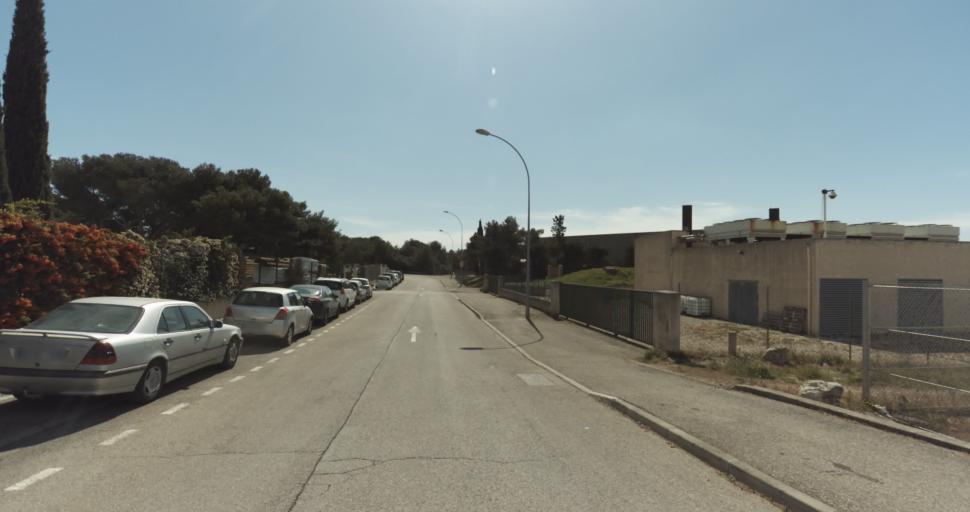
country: FR
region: Provence-Alpes-Cote d'Azur
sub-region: Departement des Bouches-du-Rhone
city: Lambesc
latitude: 43.6481
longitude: 5.2541
